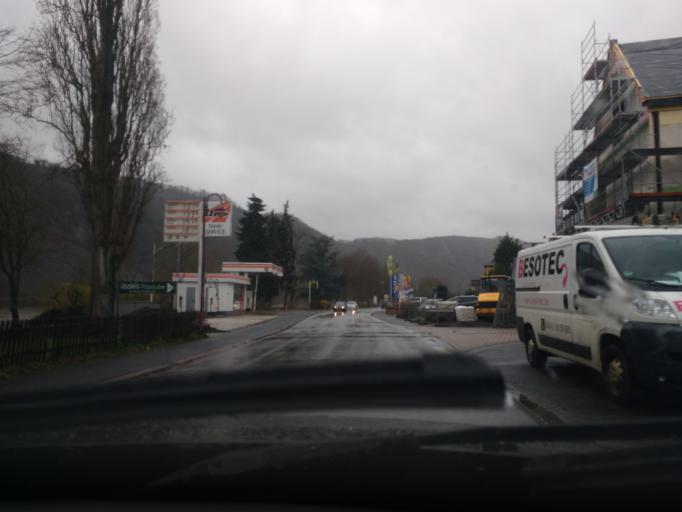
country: DE
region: Rheinland-Pfalz
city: Krov
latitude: 49.9768
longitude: 7.0877
